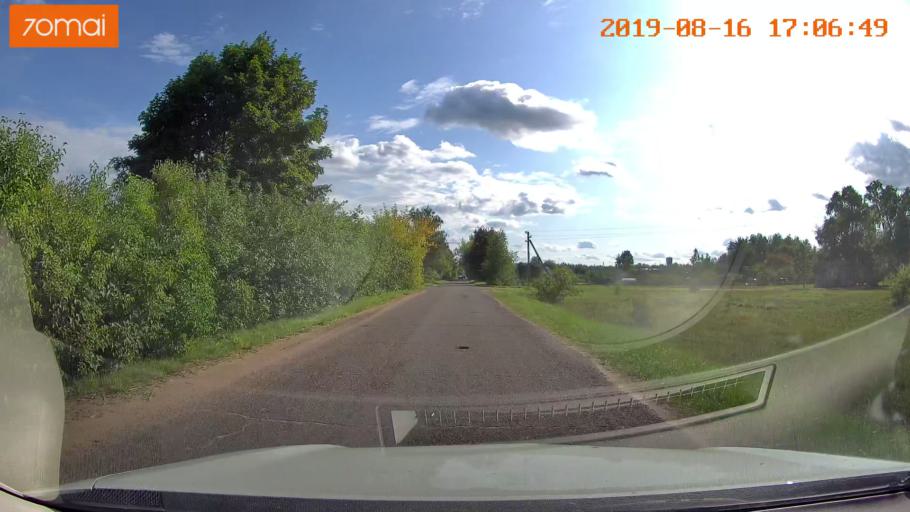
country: BY
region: Mogilev
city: Hlusha
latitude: 53.2229
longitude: 28.9289
